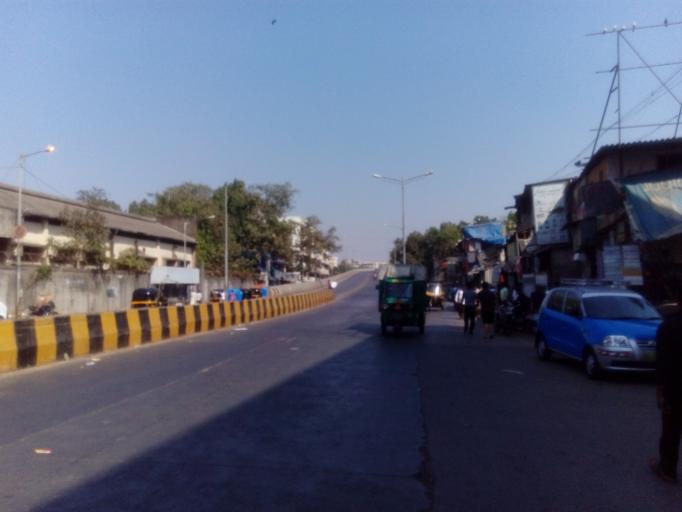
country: IN
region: Maharashtra
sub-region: Mumbai Suburban
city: Mumbai
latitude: 19.0899
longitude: 72.8394
